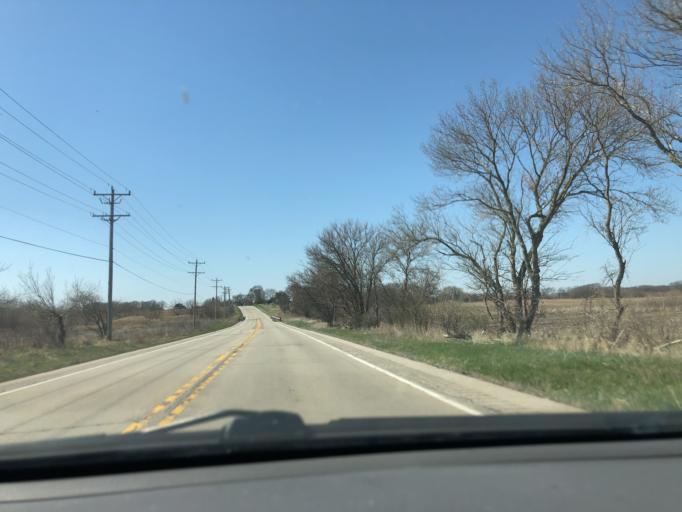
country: US
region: Illinois
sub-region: Kane County
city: Hampshire
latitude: 42.1284
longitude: -88.4884
